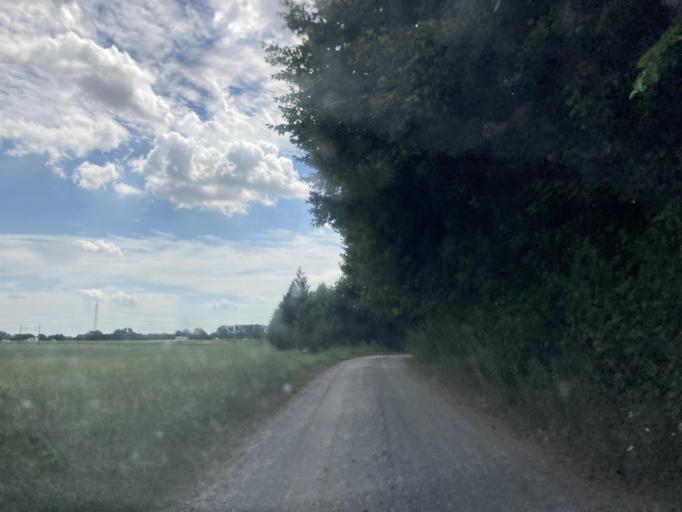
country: DK
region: Zealand
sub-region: Koge Kommune
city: Borup
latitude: 55.4602
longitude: 11.9529
